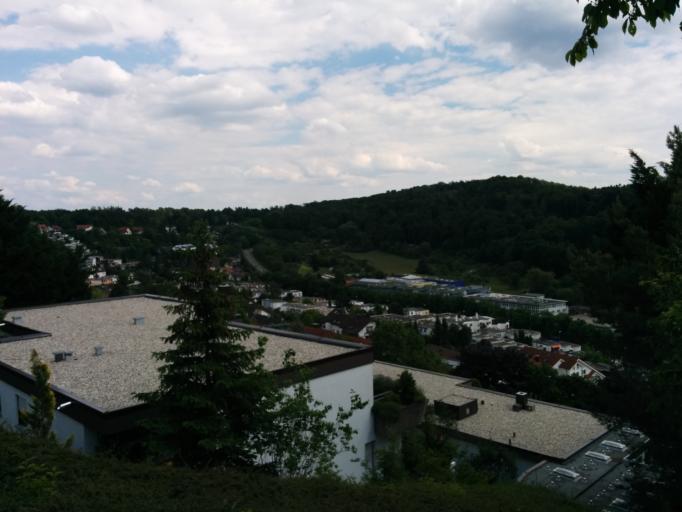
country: DE
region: Baden-Wuerttemberg
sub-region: Regierungsbezirk Stuttgart
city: Leonberg
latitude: 48.7911
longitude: 9.0269
